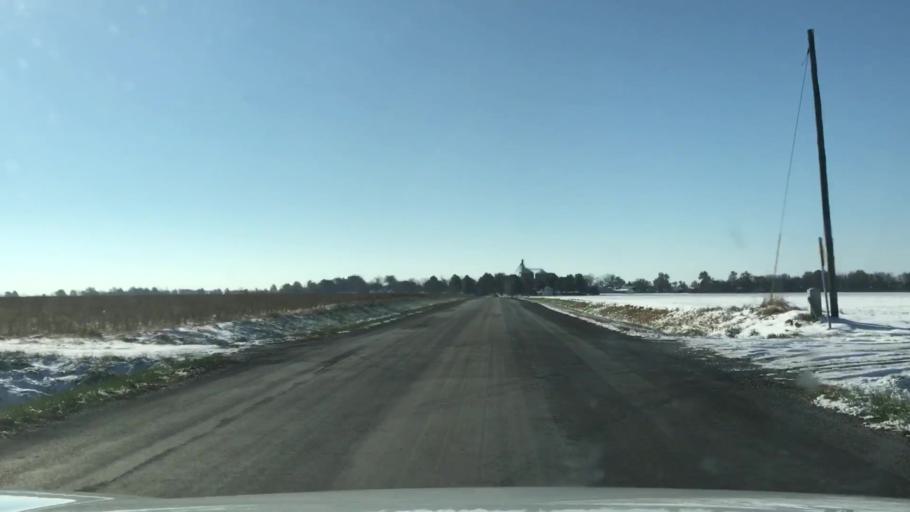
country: US
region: Illinois
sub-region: Washington County
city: Okawville
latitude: 38.4020
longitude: -89.4867
